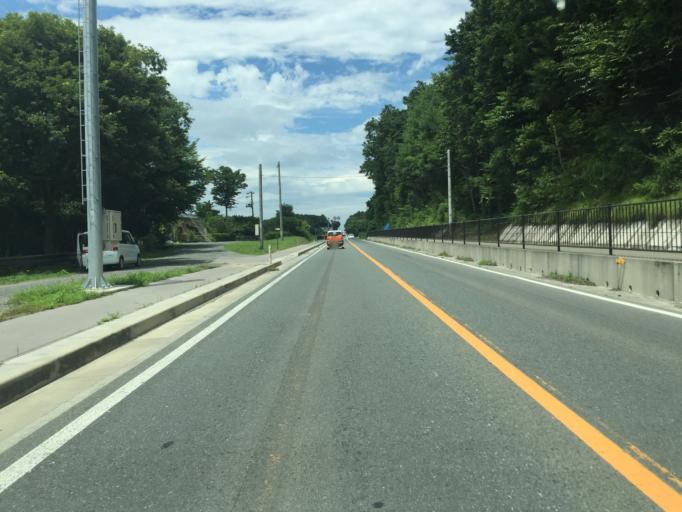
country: JP
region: Fukushima
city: Namie
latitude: 37.7312
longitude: 140.9535
